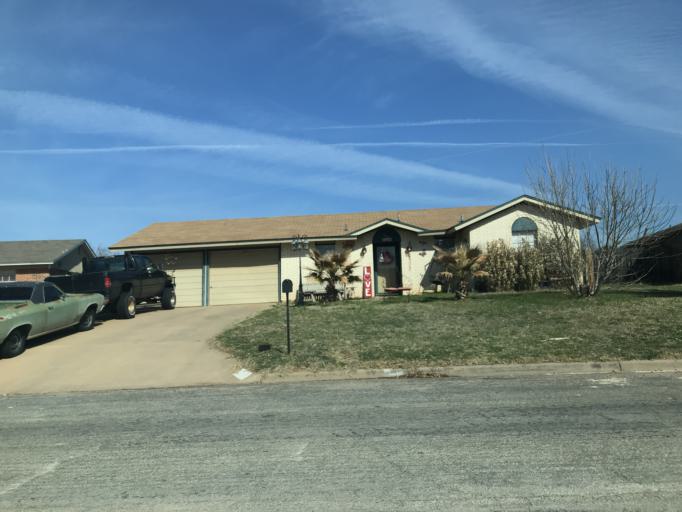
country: US
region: Texas
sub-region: Tom Green County
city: San Angelo
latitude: 31.4332
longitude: -100.4823
